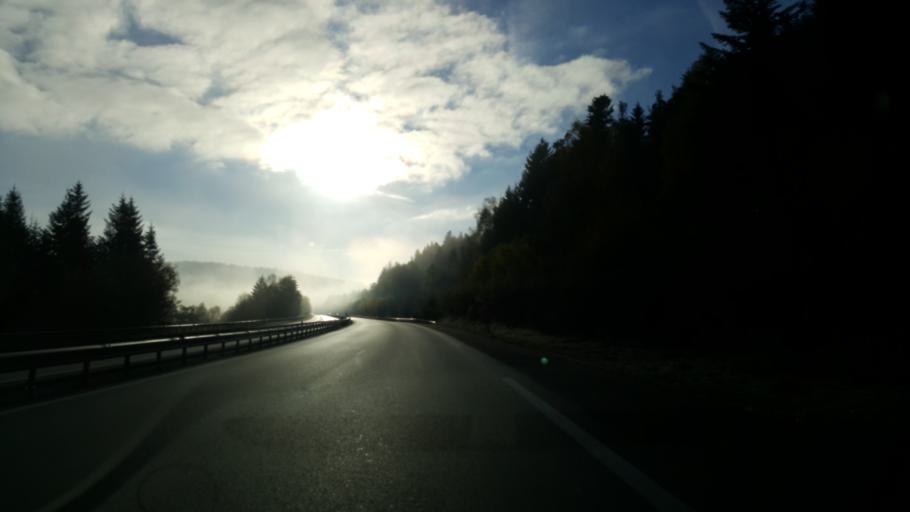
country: FR
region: Auvergne
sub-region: Departement du Puy-de-Dome
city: Chabreloche
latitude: 45.8503
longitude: 3.7295
